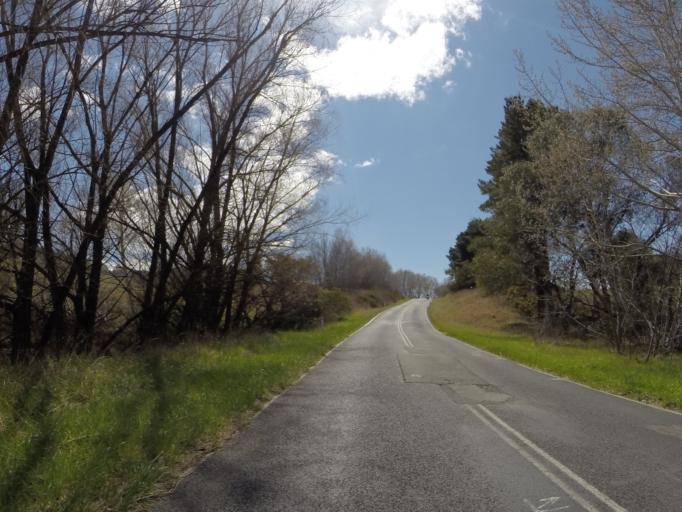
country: AU
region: Australian Capital Territory
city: Macarthur
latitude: -35.3935
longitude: 148.9605
